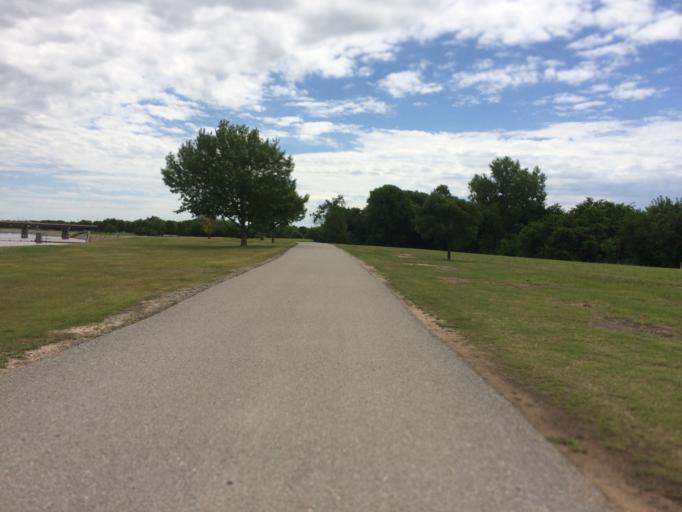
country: US
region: Oklahoma
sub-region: Oklahoma County
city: Oklahoma City
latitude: 35.4492
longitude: -97.5270
